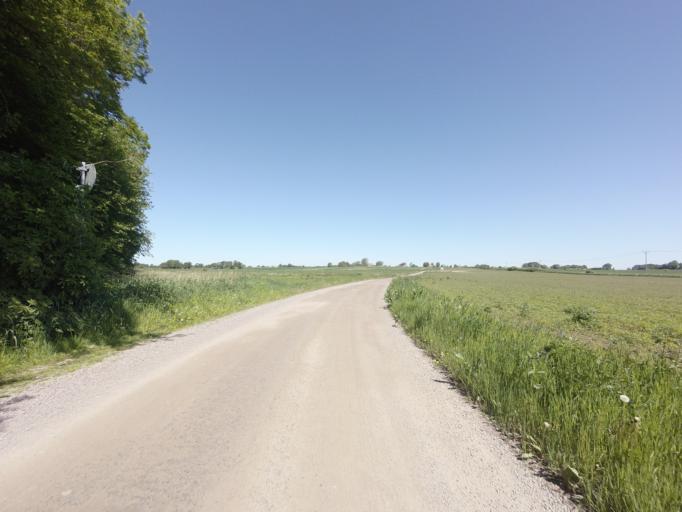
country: SE
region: Skane
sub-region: Helsingborg
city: Odakra
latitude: 56.0976
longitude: 12.7176
